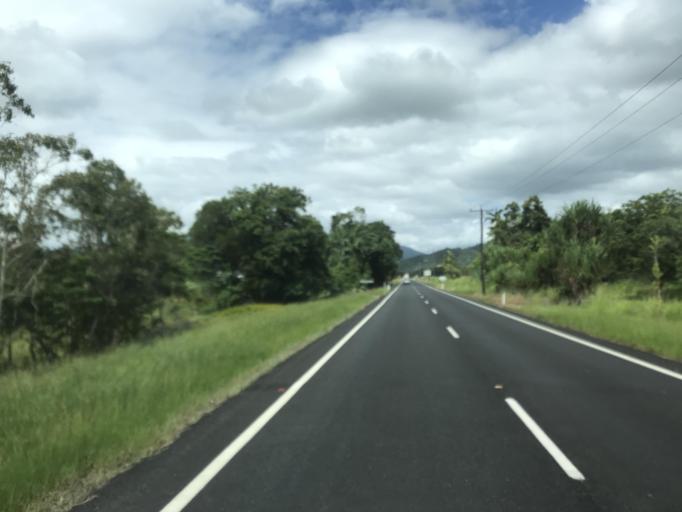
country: AU
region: Queensland
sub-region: Cassowary Coast
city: Innisfail
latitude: -17.8105
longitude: 146.0206
